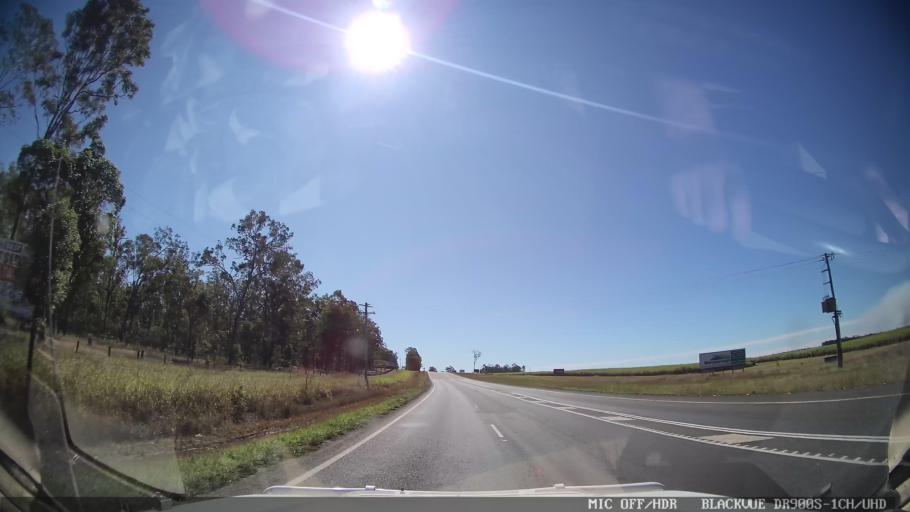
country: AU
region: Queensland
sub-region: Fraser Coast
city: Maryborough
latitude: -25.6442
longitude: 152.6379
